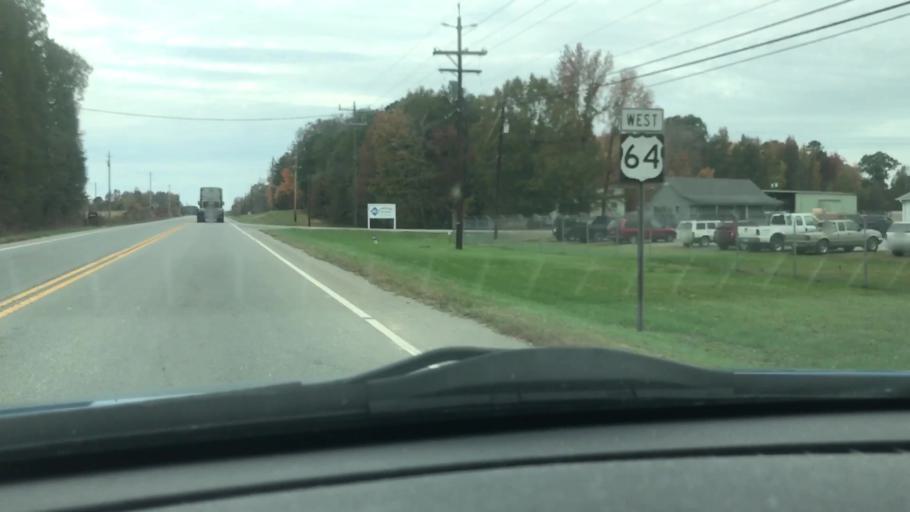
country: US
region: North Carolina
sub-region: Davidson County
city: Thomasville
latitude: 35.7817
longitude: -80.1247
